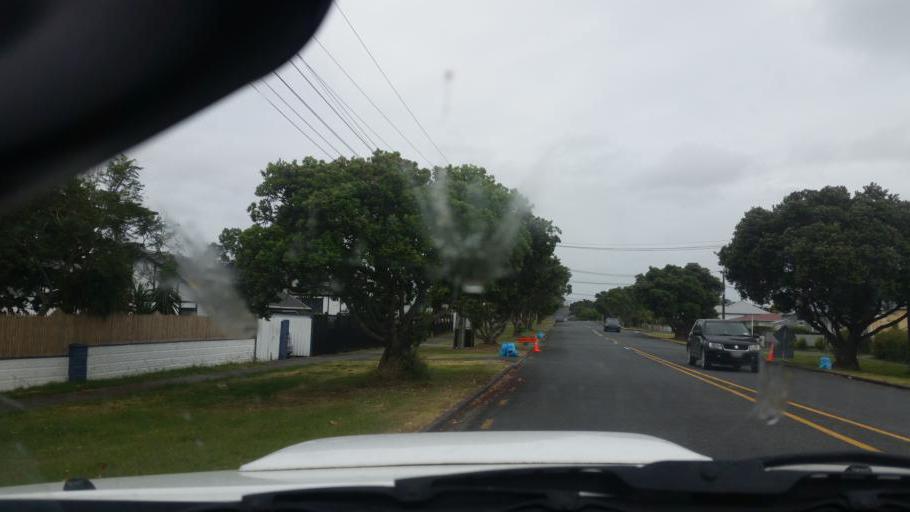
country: NZ
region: Northland
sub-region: Kaipara District
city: Dargaville
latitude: -35.9367
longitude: 173.8741
